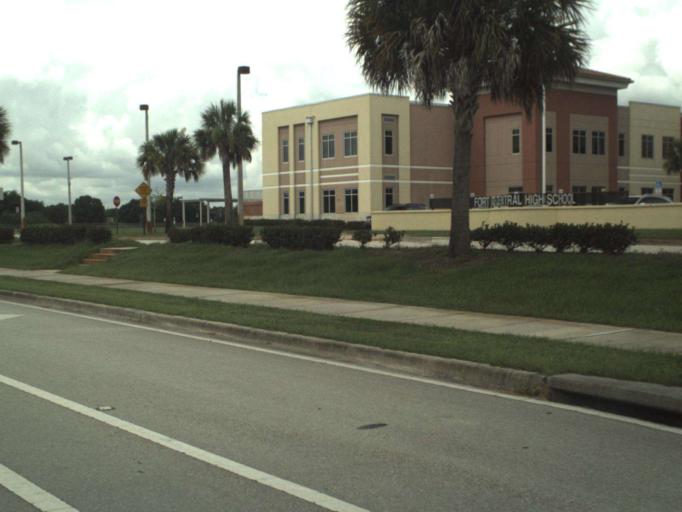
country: US
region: Florida
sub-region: Saint Lucie County
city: Fort Pierce South
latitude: 27.3913
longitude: -80.3502
